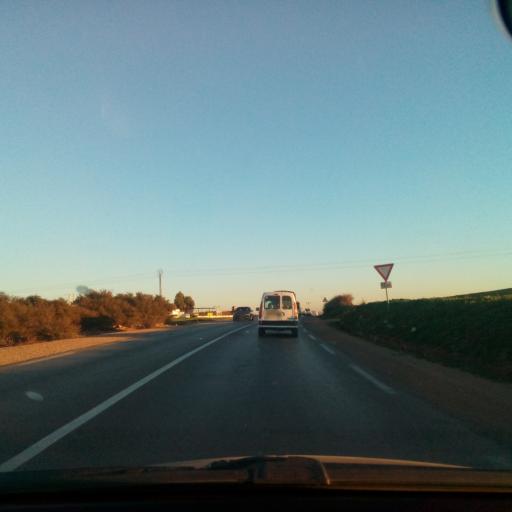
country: DZ
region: Relizane
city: Relizane
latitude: 35.7342
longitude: 0.2987
